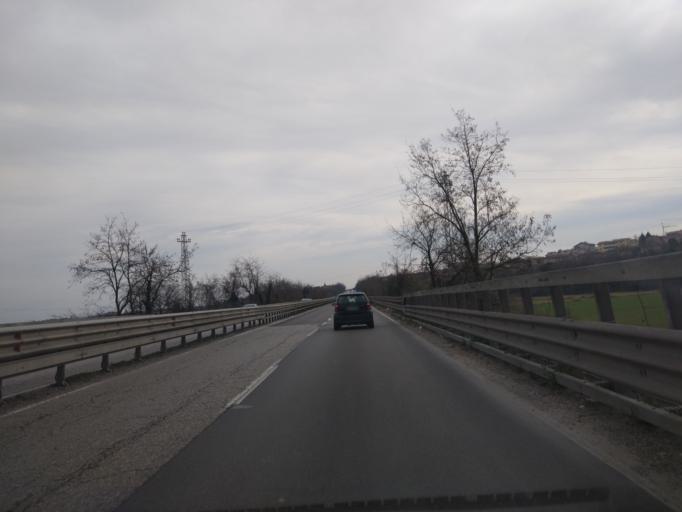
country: IT
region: Veneto
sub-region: Provincia di Verona
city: Bussolengo
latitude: 45.4752
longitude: 10.8612
